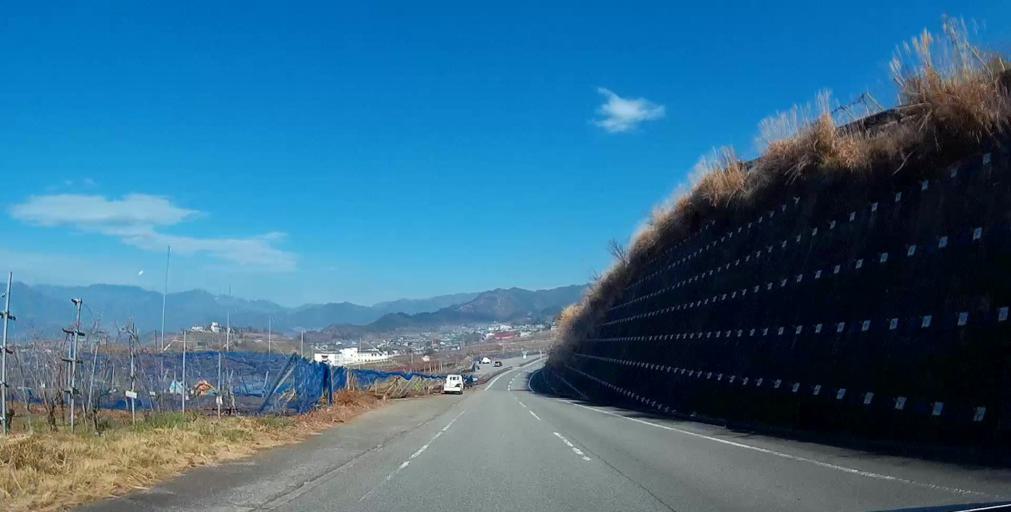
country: JP
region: Yamanashi
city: Enzan
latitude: 35.6626
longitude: 138.7380
